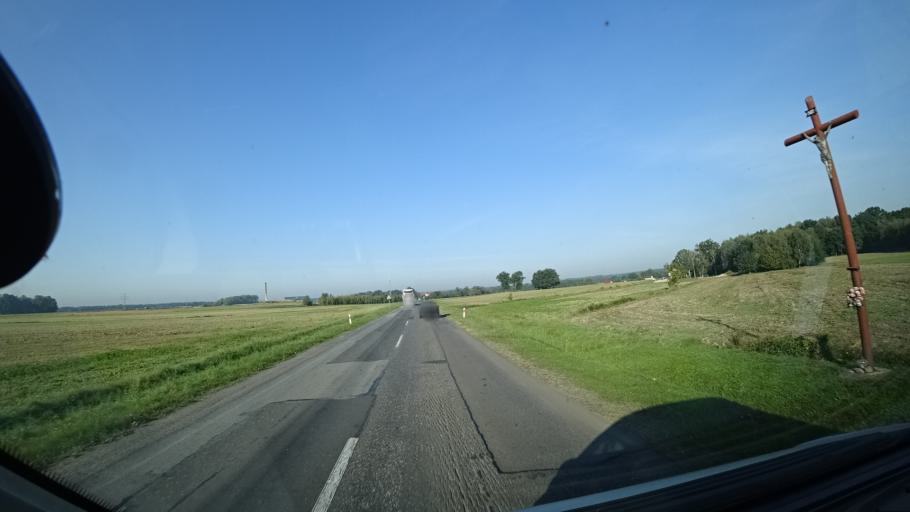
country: PL
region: Silesian Voivodeship
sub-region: Powiat gliwicki
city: Sosnicowice
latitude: 50.2795
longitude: 18.4857
